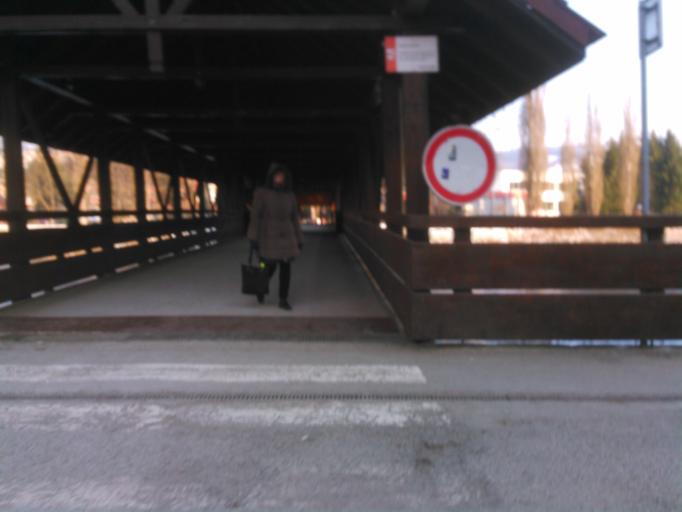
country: SK
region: Zilinsky
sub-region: Okres Dolny Kubin
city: Dolny Kubin
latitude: 49.2103
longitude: 19.2907
